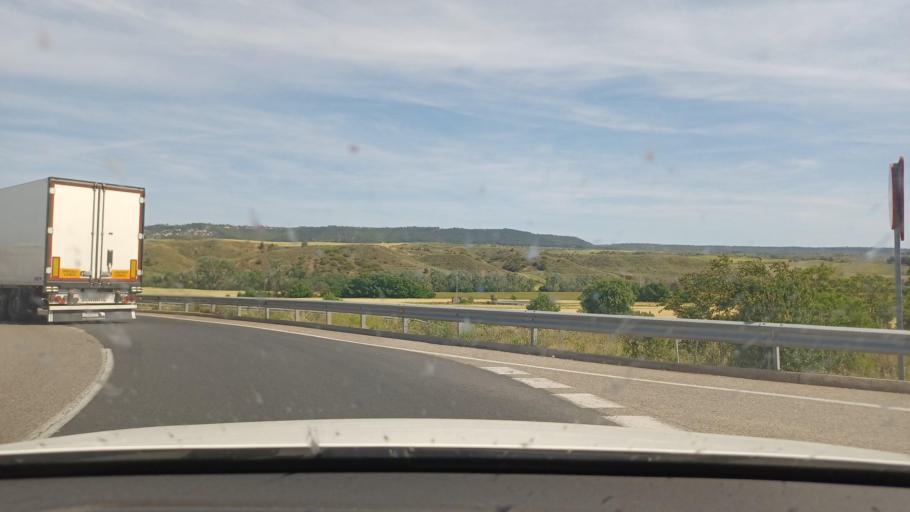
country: ES
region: Castille-La Mancha
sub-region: Provincia de Guadalajara
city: Cabanillas del Campo
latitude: 40.6179
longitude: -3.2015
